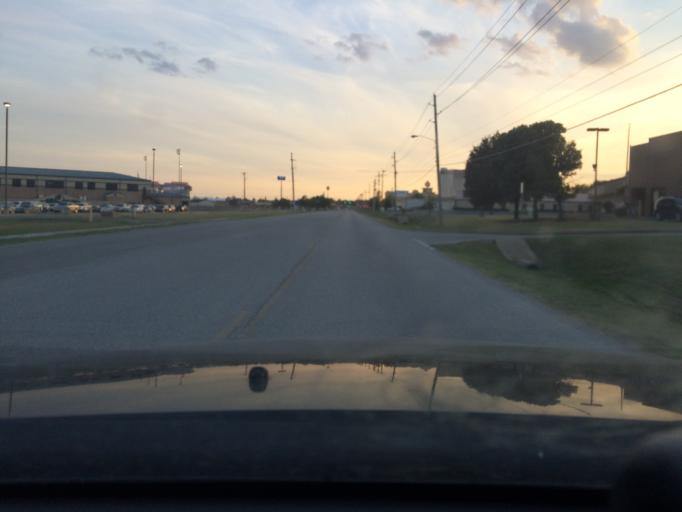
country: US
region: Oklahoma
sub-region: Rogers County
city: Catoosa
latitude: 36.1718
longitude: -95.7565
